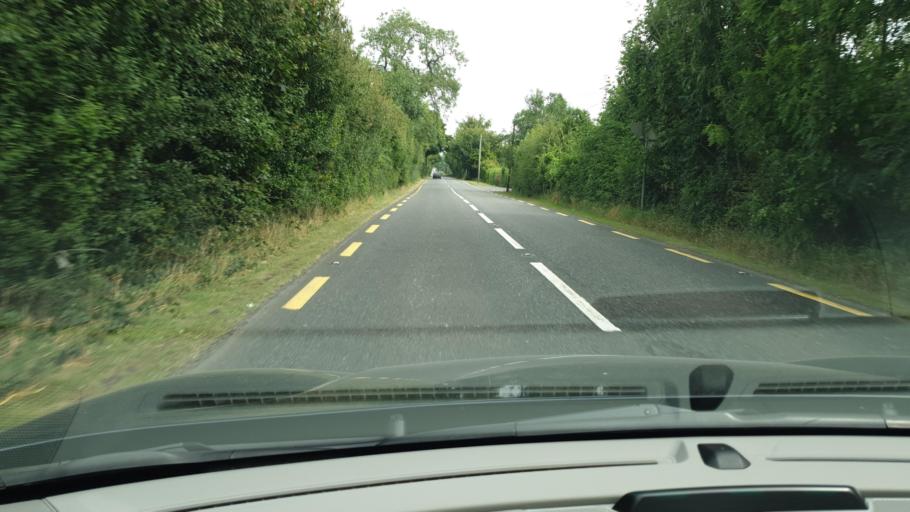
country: IE
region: Leinster
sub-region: An Mhi
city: Athboy
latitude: 53.6719
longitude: -6.9646
